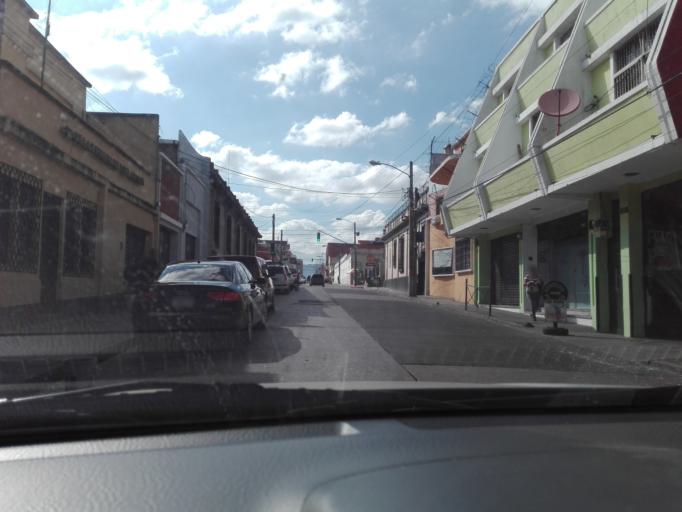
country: GT
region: Guatemala
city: Guatemala City
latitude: 14.6440
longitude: -90.5099
